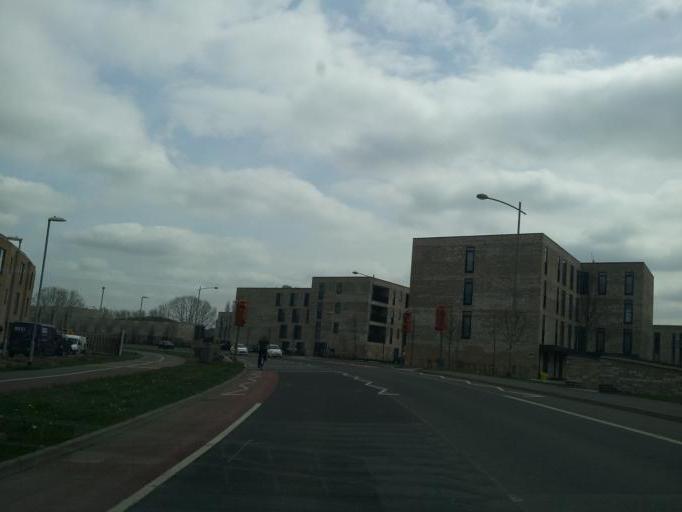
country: GB
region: England
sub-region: Cambridgeshire
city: Cambridge
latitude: 52.1669
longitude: 0.1224
